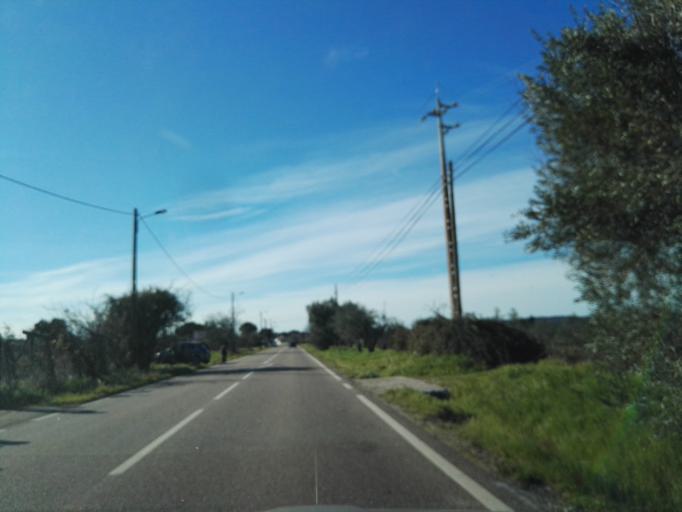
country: PT
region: Portalegre
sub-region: Gaviao
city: Gaviao
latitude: 39.4616
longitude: -8.0309
